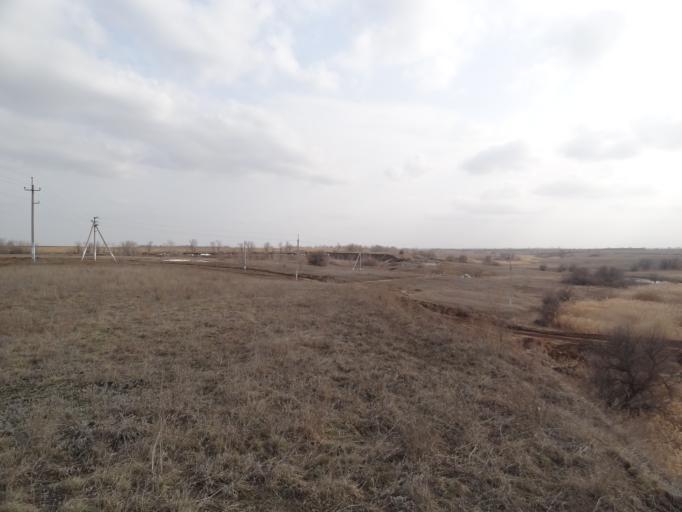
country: RU
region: Saratov
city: Shumeyka
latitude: 51.4883
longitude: 46.2816
